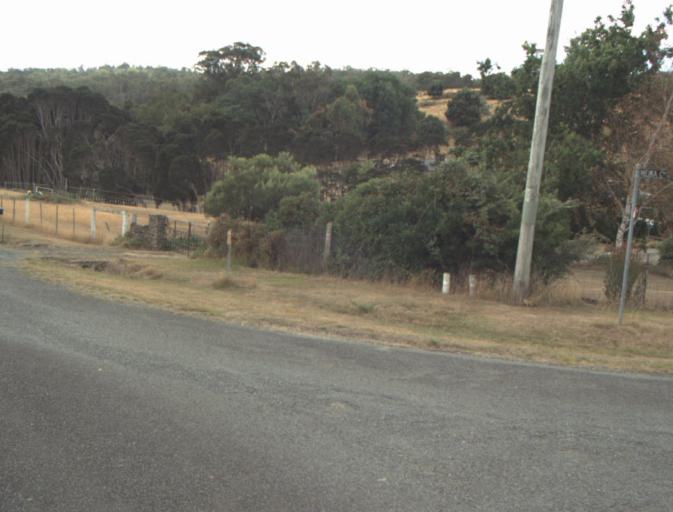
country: AU
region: Tasmania
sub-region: Launceston
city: Mayfield
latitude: -41.2796
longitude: 147.0182
